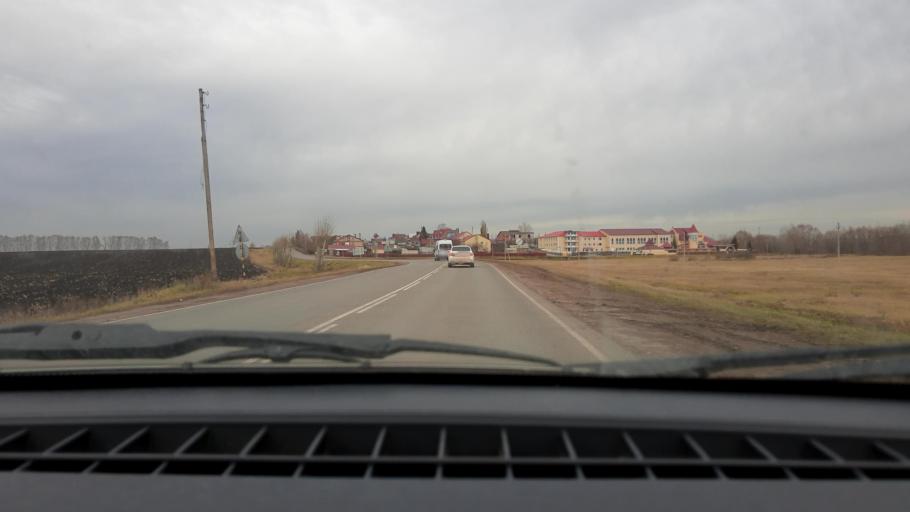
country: RU
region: Bashkortostan
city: Ufa
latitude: 54.8173
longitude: 55.9819
